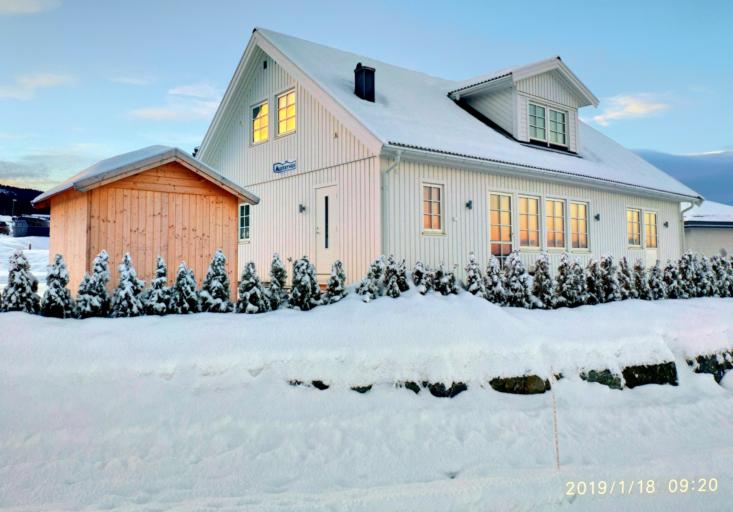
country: NO
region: Buskerud
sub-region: Modum
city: Vikersund
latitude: 59.8980
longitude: 9.9422
